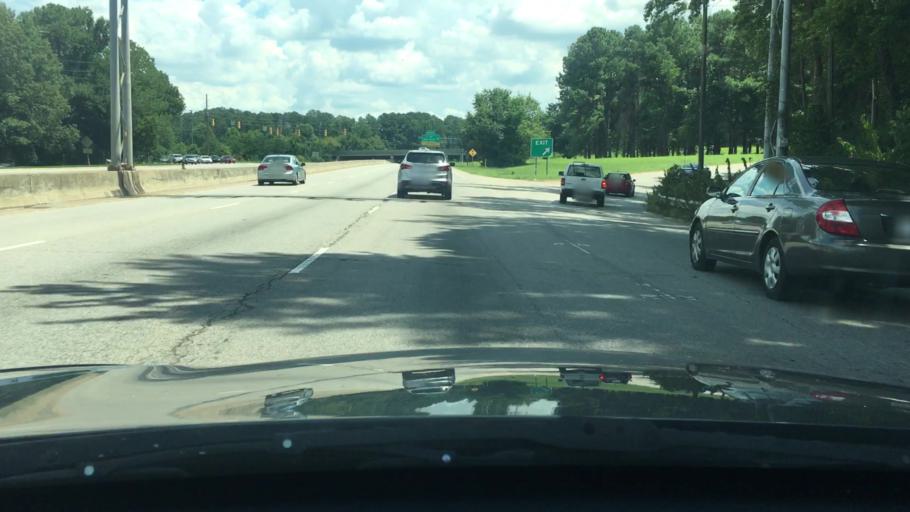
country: US
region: North Carolina
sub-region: Wake County
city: West Raleigh
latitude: 35.8371
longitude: -78.6724
